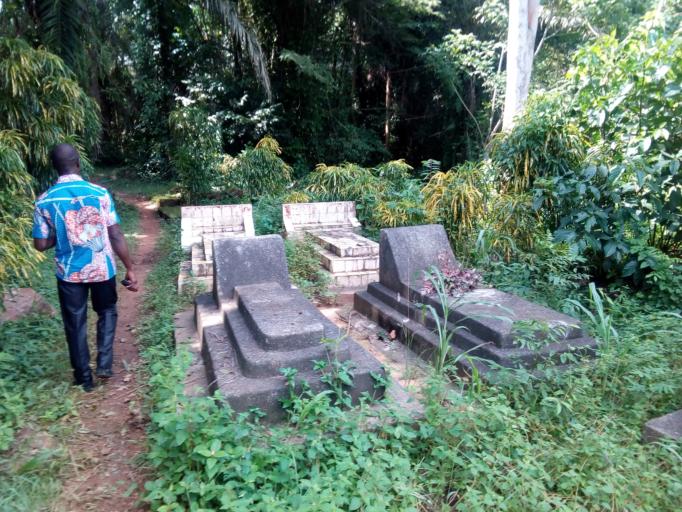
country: CI
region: Sud-Comoe
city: Mafere
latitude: 5.2967
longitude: -2.7862
